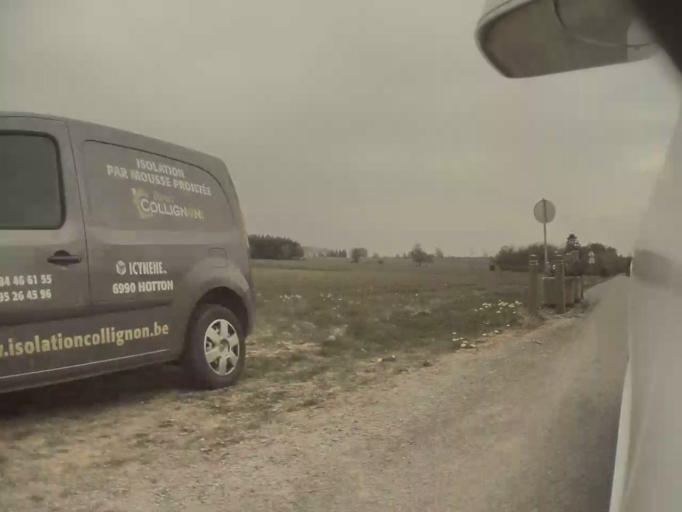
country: BE
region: Wallonia
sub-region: Province du Luxembourg
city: La Roche-en-Ardenne
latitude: 50.2312
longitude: 5.6166
